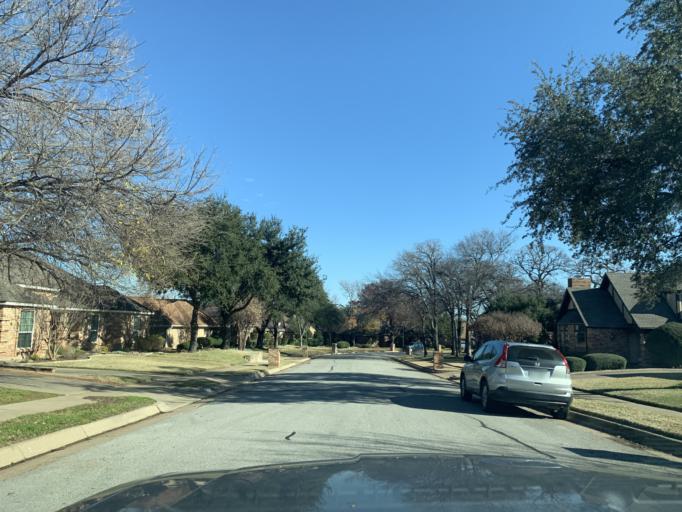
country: US
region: Texas
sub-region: Tarrant County
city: Bedford
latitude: 32.8469
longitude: -97.1573
